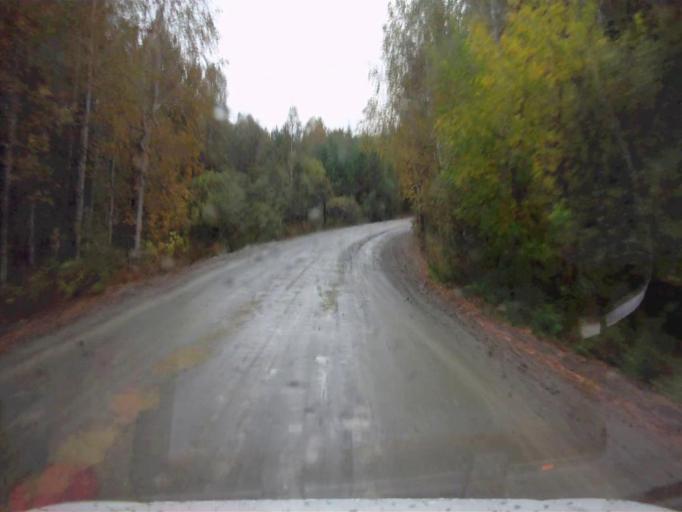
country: RU
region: Chelyabinsk
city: Kyshtym
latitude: 55.7475
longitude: 60.4901
